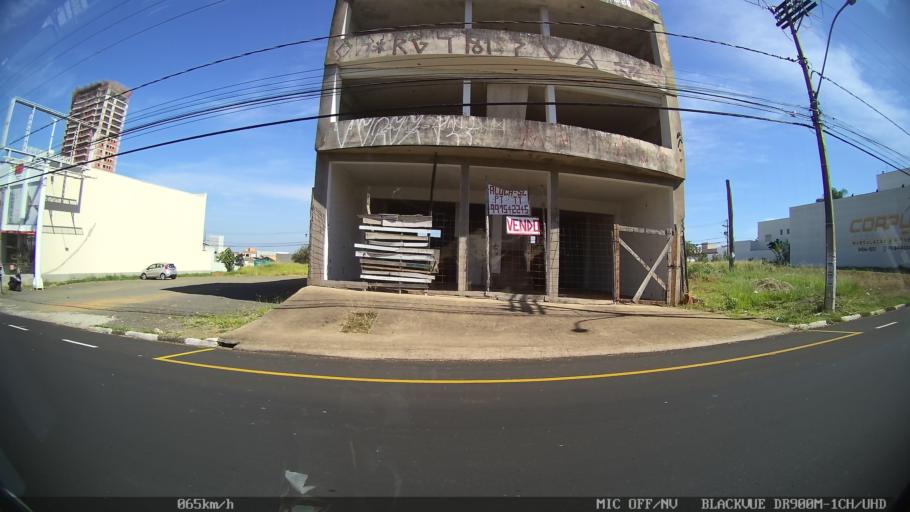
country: BR
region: Sao Paulo
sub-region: Franca
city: Franca
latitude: -20.5508
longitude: -47.4157
